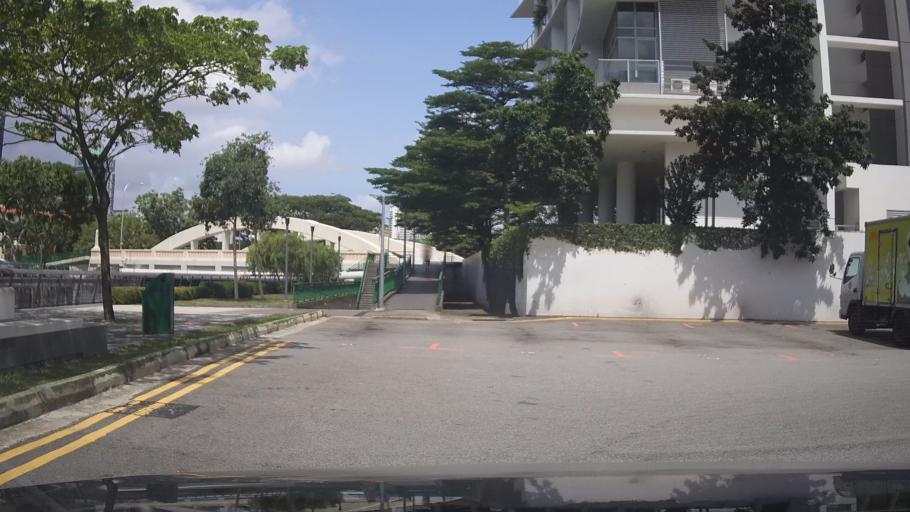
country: SG
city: Singapore
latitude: 1.3063
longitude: 103.8637
